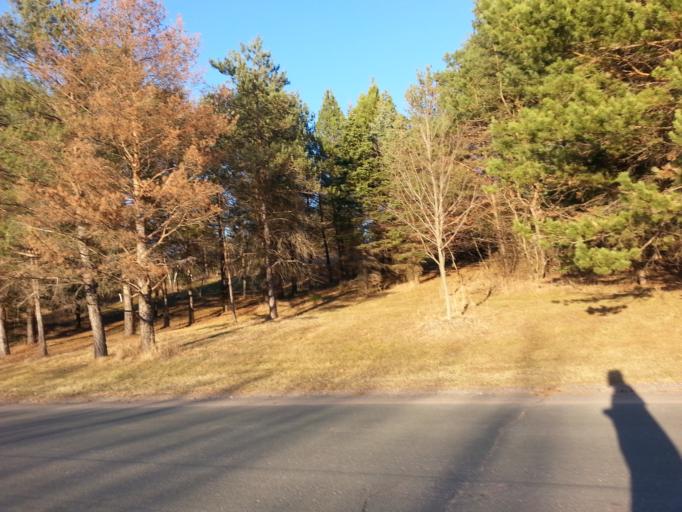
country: US
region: Minnesota
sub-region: Washington County
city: Lake Elmo
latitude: 44.9820
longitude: -92.8306
